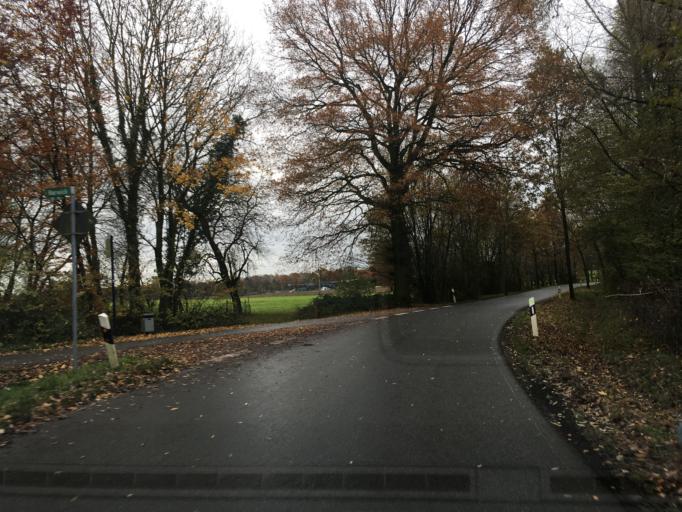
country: DE
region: North Rhine-Westphalia
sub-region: Regierungsbezirk Munster
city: Gescher
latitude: 51.9758
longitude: 7.0081
